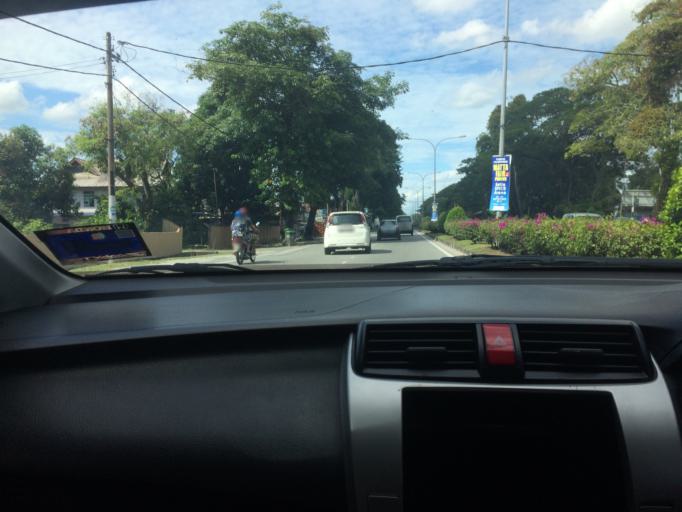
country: MY
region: Kedah
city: Alor Setar
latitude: 6.1226
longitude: 100.3824
